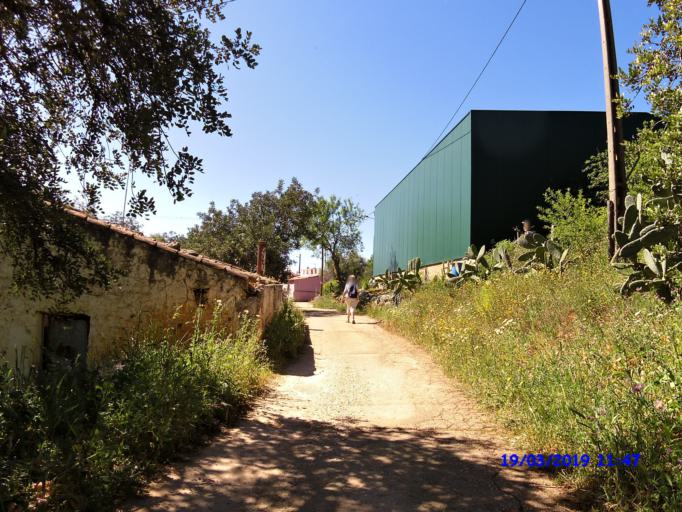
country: PT
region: Faro
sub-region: Loule
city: Boliqueime
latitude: 37.2104
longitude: -8.1459
